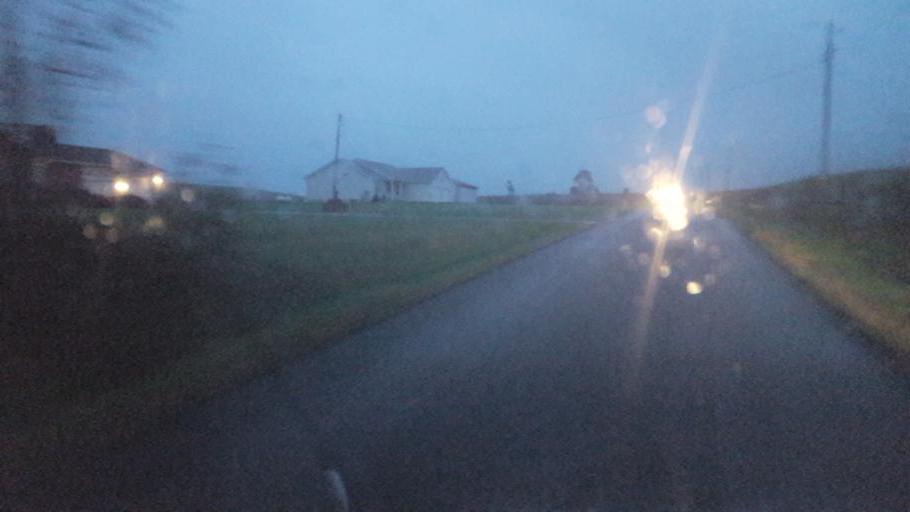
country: US
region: Ohio
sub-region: Richland County
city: Lexington
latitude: 40.6011
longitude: -82.6278
